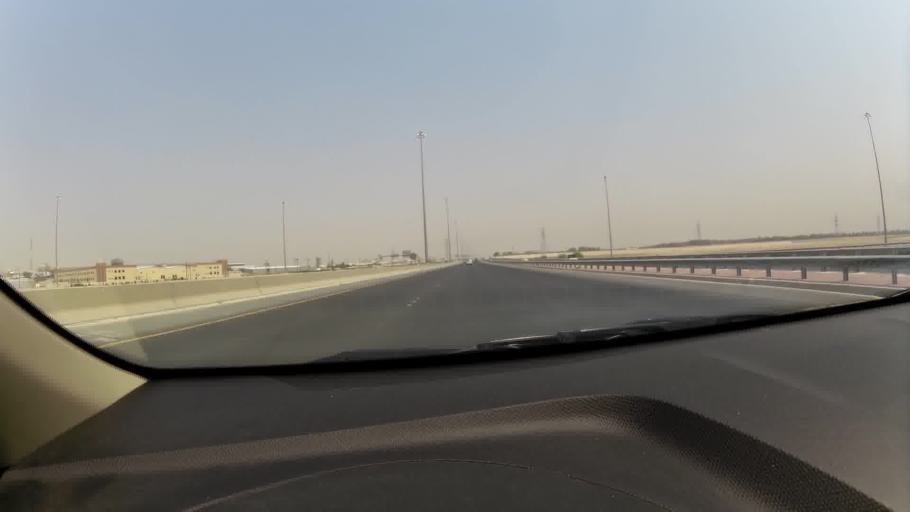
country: KW
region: Muhafazat al Jahra'
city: Al Jahra'
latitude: 29.2950
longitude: 47.7364
